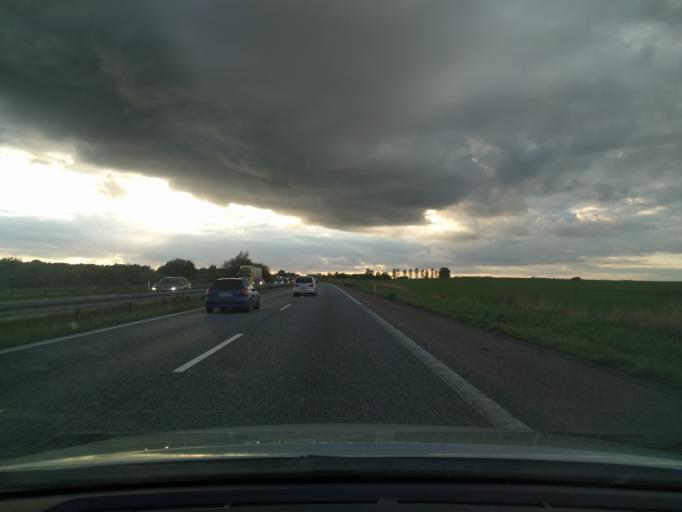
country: DK
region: Zealand
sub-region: Slagelse Kommune
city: Slagelse
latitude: 55.4296
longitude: 11.4426
